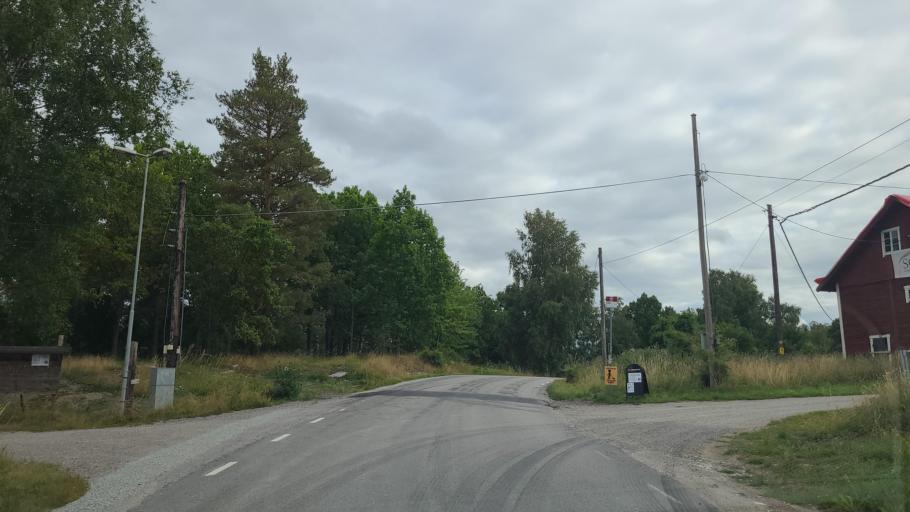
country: SE
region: Stockholm
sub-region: Upplands-Bro Kommun
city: Bro
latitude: 59.4877
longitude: 17.6036
